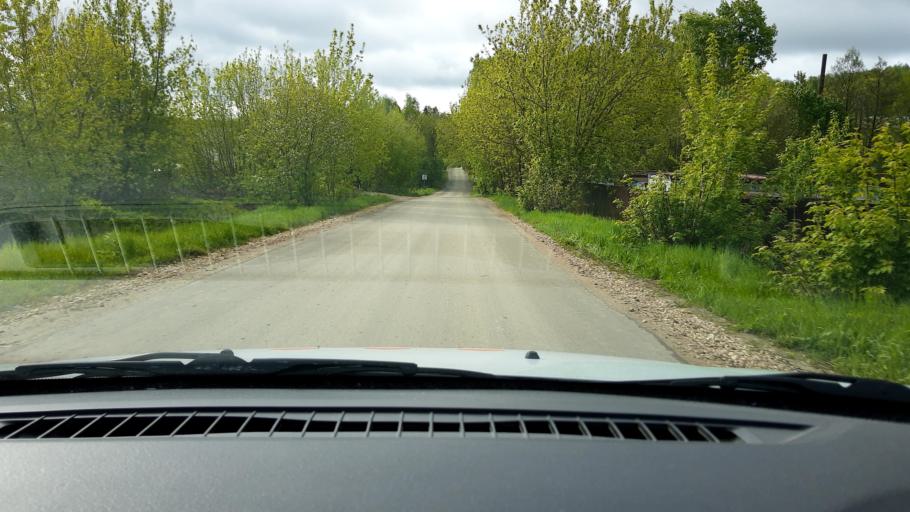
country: RU
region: Nizjnij Novgorod
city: Afonino
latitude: 56.1907
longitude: 44.0741
